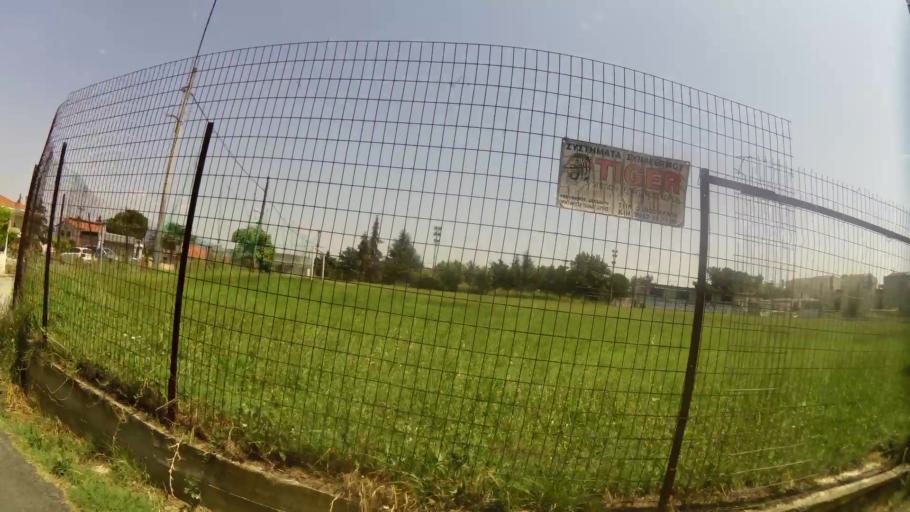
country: GR
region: Central Macedonia
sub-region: Nomos Thessalonikis
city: Plagiari
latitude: 40.4784
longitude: 22.9561
